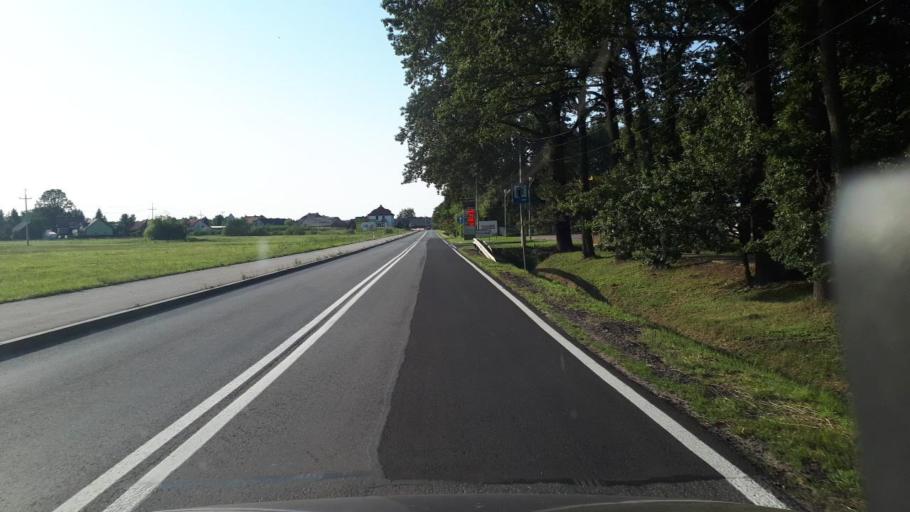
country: PL
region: Silesian Voivodeship
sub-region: Powiat lubliniecki
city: Sierakow Slaski
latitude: 50.7984
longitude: 18.5796
